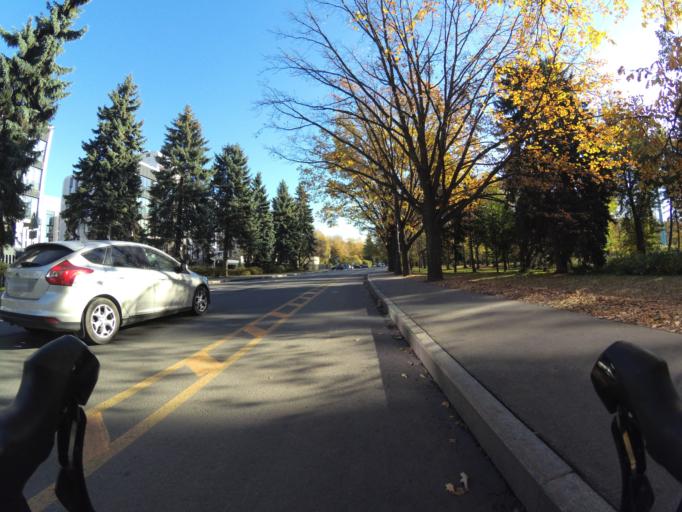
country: RU
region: Leningrad
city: Krestovskiy ostrov
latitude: 59.9746
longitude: 30.2466
